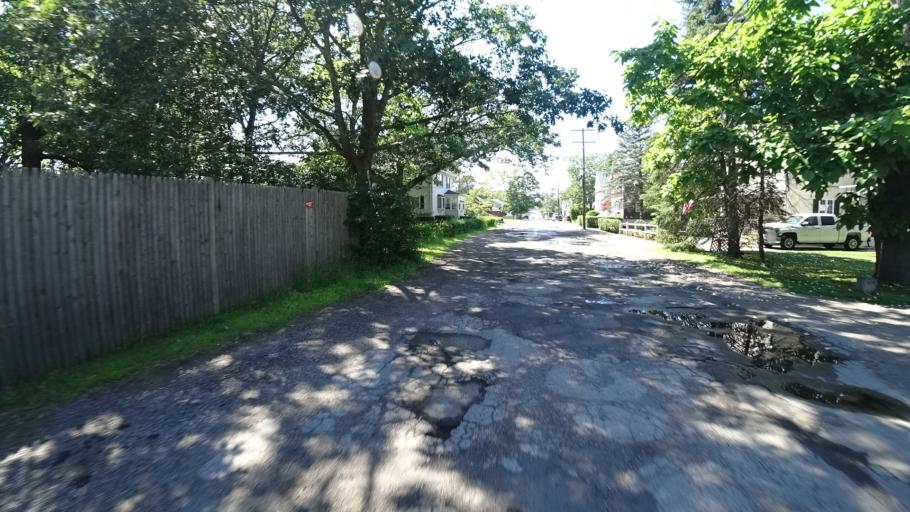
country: US
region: Massachusetts
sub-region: Norfolk County
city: Dedham
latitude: 42.2409
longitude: -71.1481
